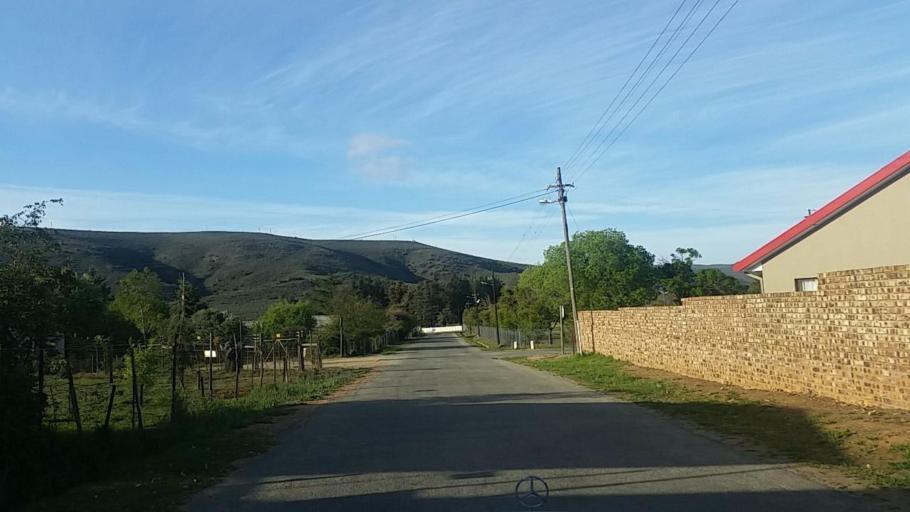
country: ZA
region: Western Cape
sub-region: Eden District Municipality
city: Knysna
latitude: -33.6578
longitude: 23.1215
